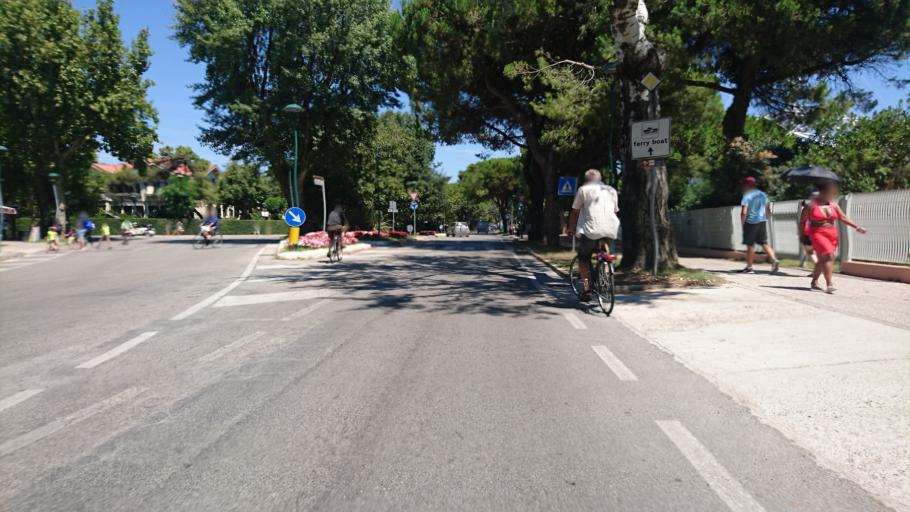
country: IT
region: Veneto
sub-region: Provincia di Venezia
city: Lido
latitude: 45.4142
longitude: 12.3759
